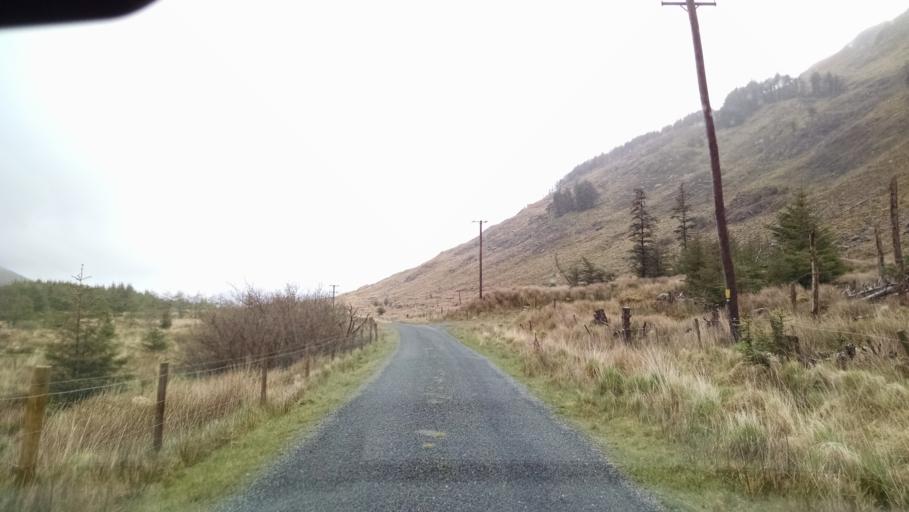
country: IE
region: Connaught
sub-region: Maigh Eo
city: Westport
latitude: 53.6430
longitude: -9.6958
